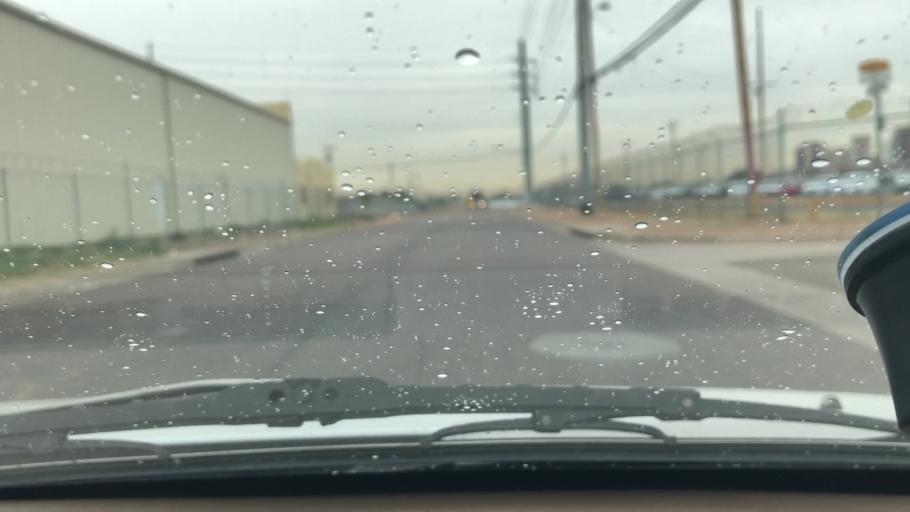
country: US
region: Arizona
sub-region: Maricopa County
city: Phoenix
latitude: 33.4392
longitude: -112.0554
